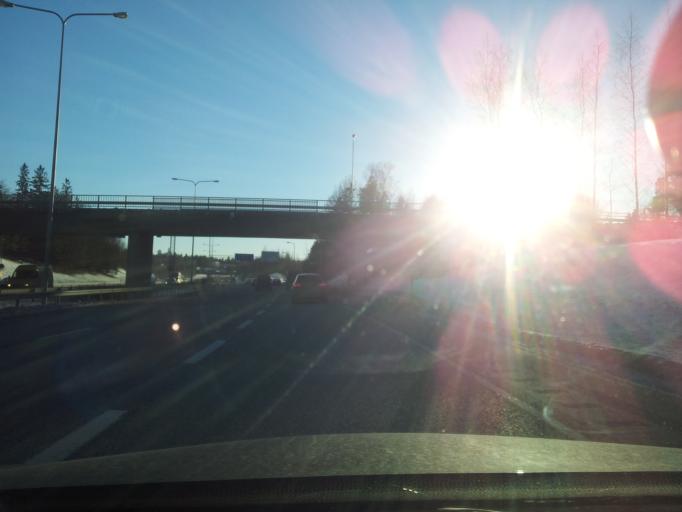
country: FI
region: Uusimaa
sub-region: Helsinki
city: Espoo
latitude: 60.2152
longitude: 24.6336
